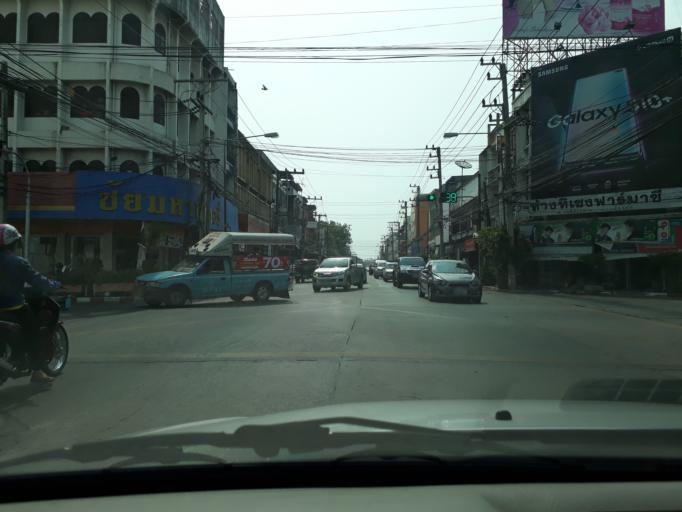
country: TH
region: Khon Kaen
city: Khon Kaen
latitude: 16.4301
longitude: 102.8374
